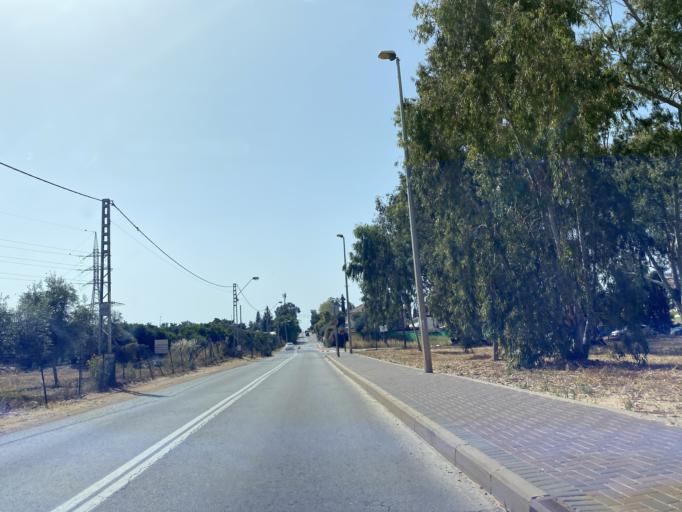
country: IL
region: Central District
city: Ra'anana
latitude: 32.1729
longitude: 34.8776
